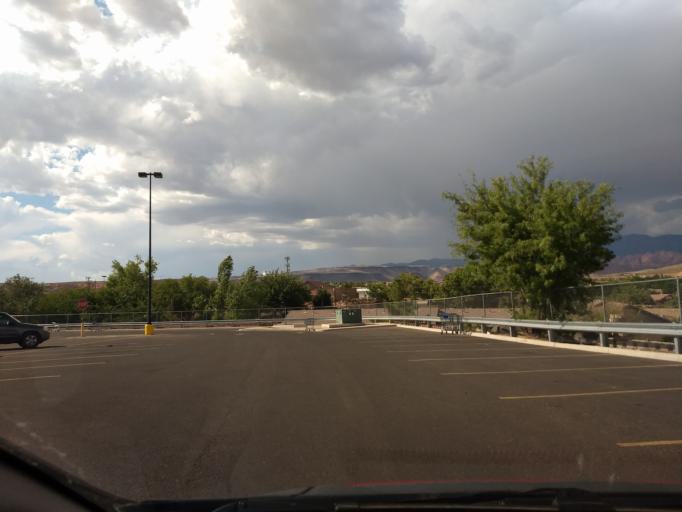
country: US
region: Utah
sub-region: Washington County
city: Washington
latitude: 37.1273
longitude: -113.5168
